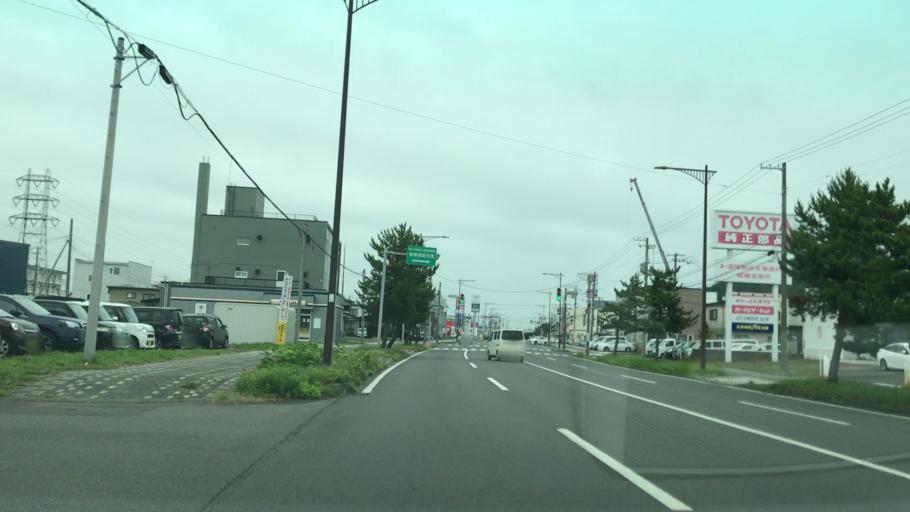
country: JP
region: Hokkaido
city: Muroran
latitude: 42.3503
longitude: 141.0386
